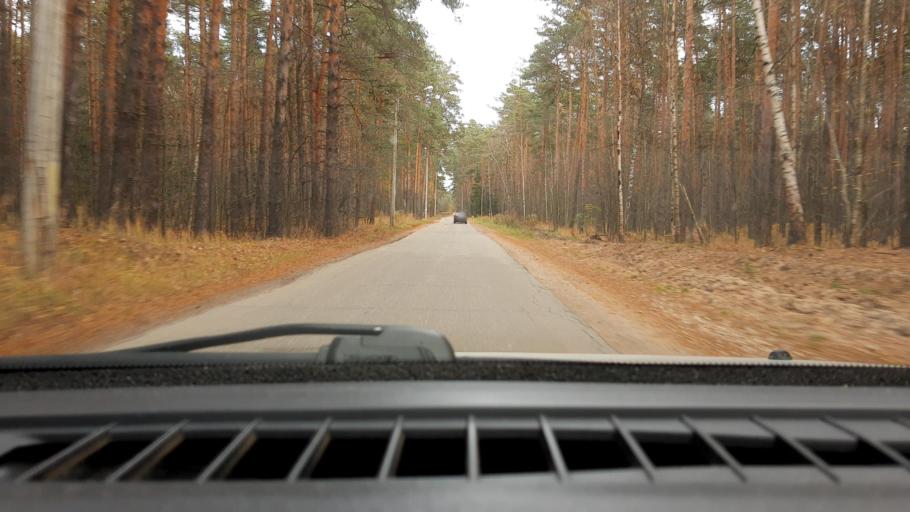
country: RU
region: Nizjnij Novgorod
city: Kstovo
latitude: 56.1685
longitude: 44.1063
